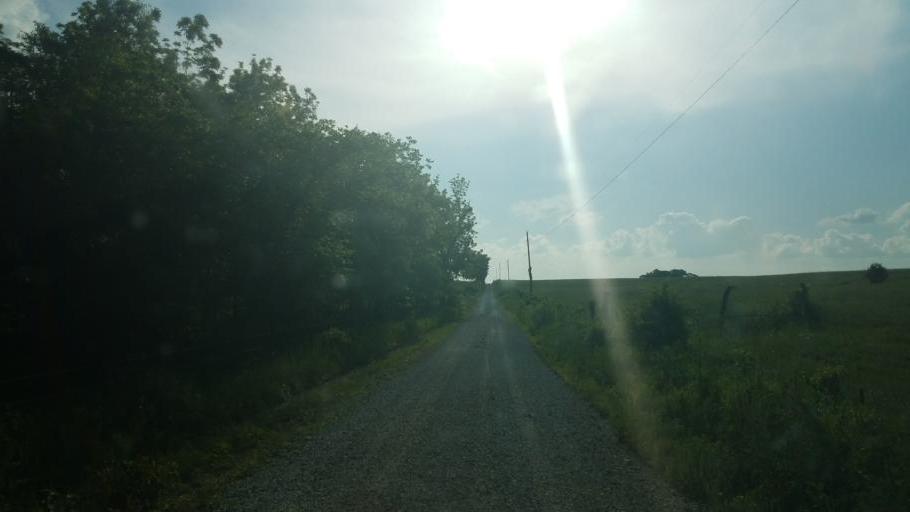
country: US
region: Missouri
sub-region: Moniteau County
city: California
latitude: 38.7527
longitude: -92.6092
